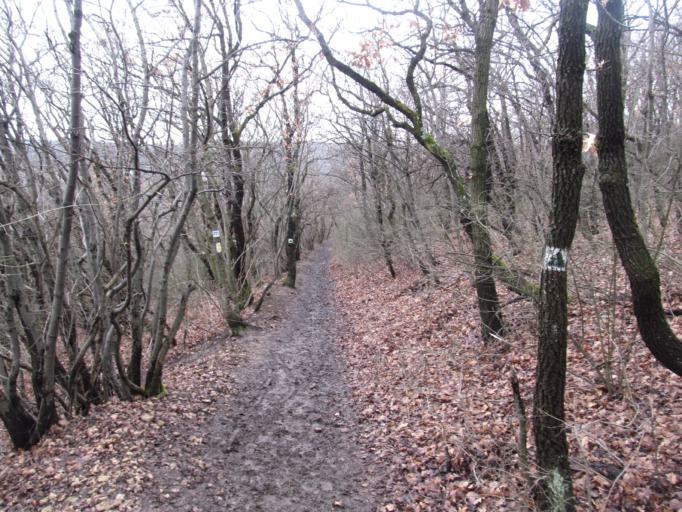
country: HU
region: Pest
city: Budaors
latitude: 47.4885
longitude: 18.9793
